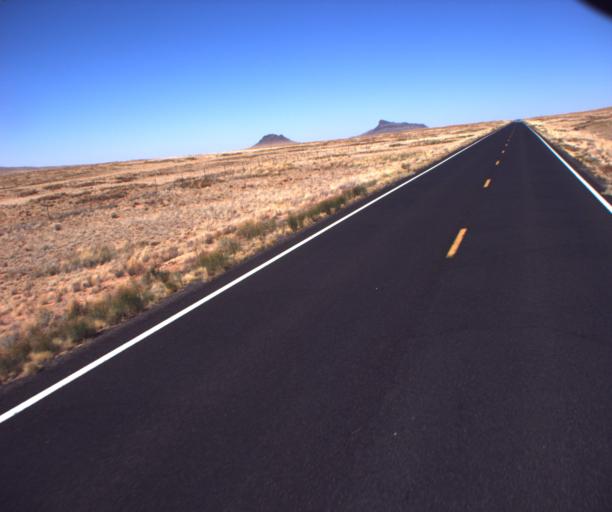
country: US
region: Arizona
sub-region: Navajo County
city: Dilkon
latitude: 35.3980
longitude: -110.4260
